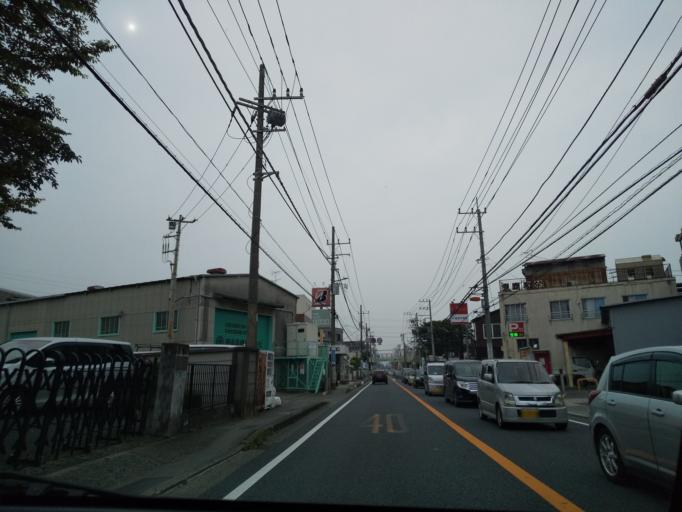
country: JP
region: Kanagawa
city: Minami-rinkan
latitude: 35.5043
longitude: 139.4213
